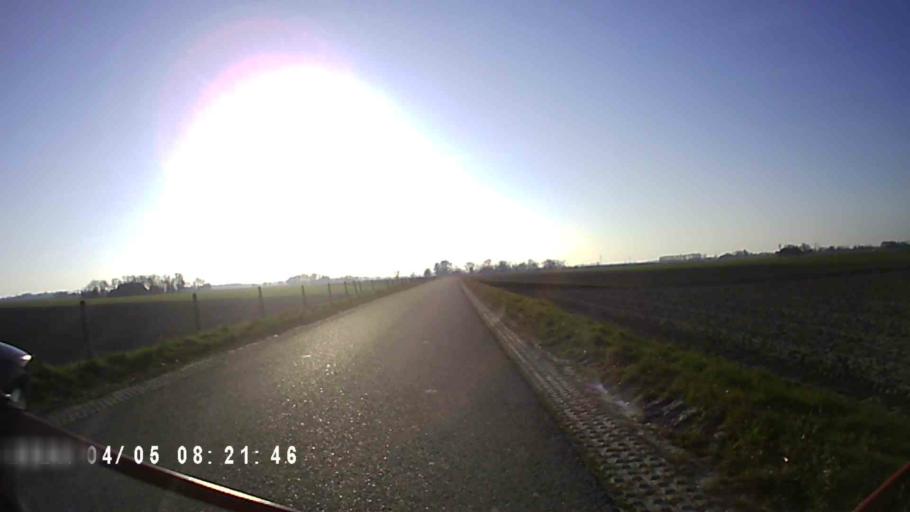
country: NL
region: Groningen
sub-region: Gemeente Zuidhorn
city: Oldehove
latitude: 53.3311
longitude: 6.4538
